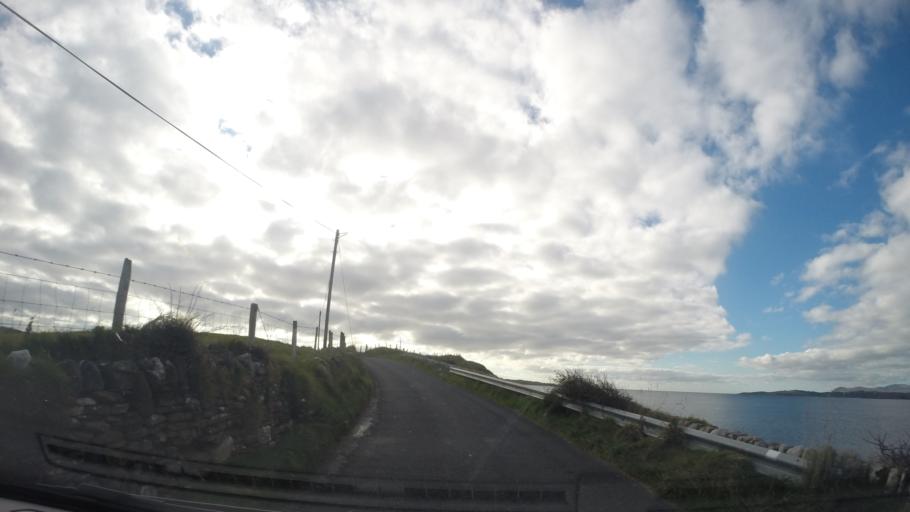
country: IE
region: Ulster
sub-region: County Donegal
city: Killybegs
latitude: 54.6134
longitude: -8.3764
